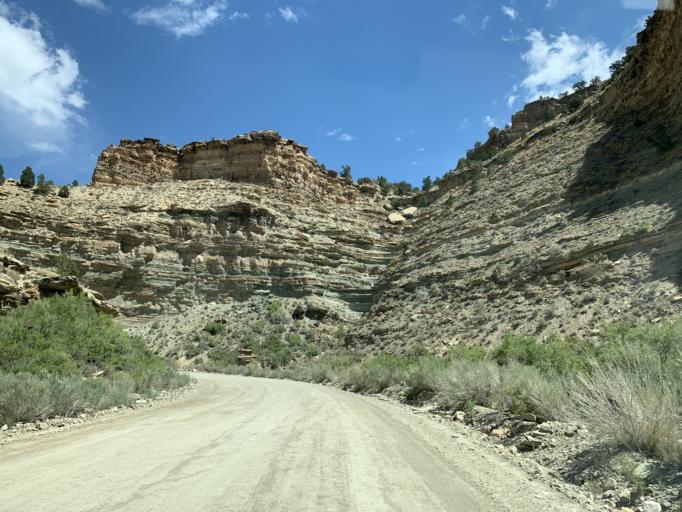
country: US
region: Utah
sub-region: Carbon County
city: East Carbon City
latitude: 39.8274
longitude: -110.2473
